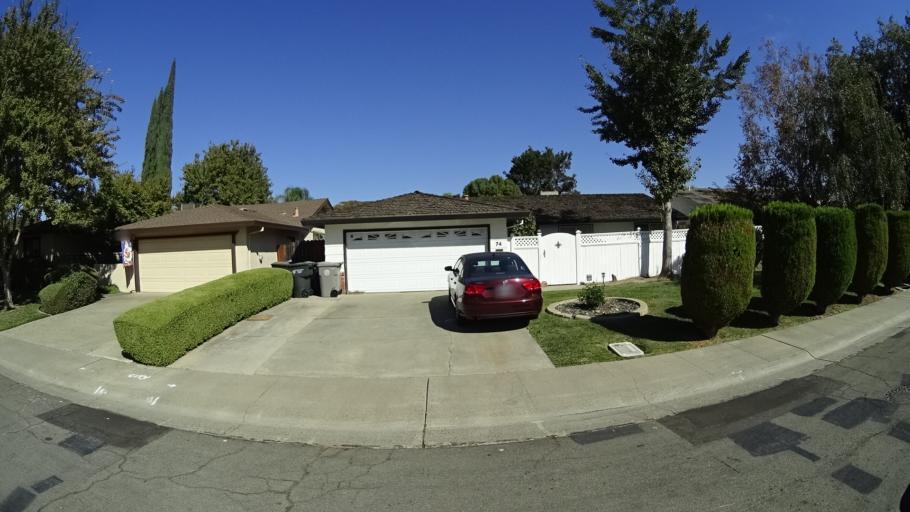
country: US
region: California
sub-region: Sacramento County
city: Parkway
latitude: 38.5011
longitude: -121.5241
